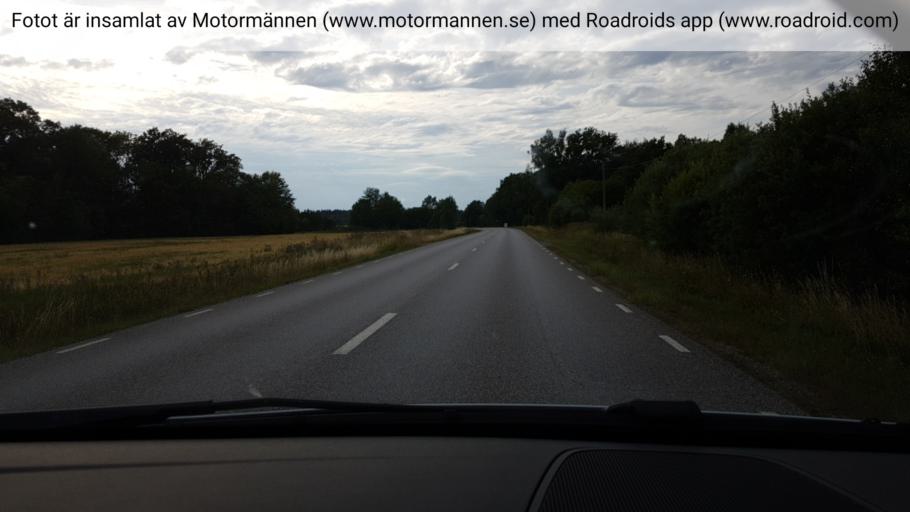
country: SE
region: Stockholm
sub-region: Norrtalje Kommun
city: Skanninge
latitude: 59.8964
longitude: 18.3959
